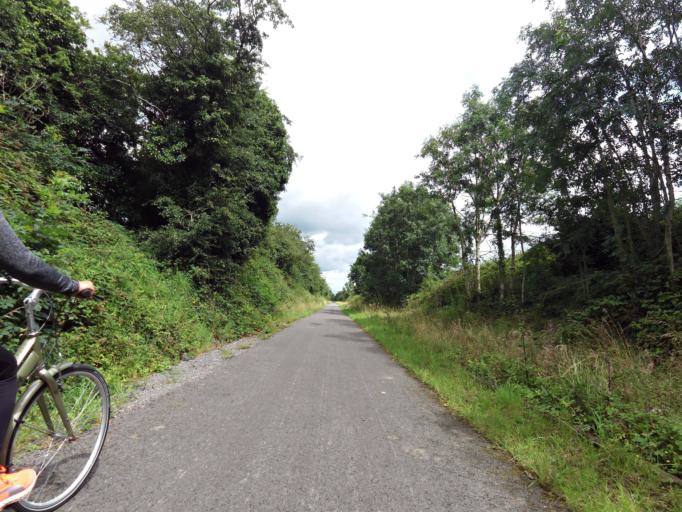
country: IE
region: Leinster
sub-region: An Iarmhi
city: An Muileann gCearr
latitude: 53.4928
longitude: -7.4503
